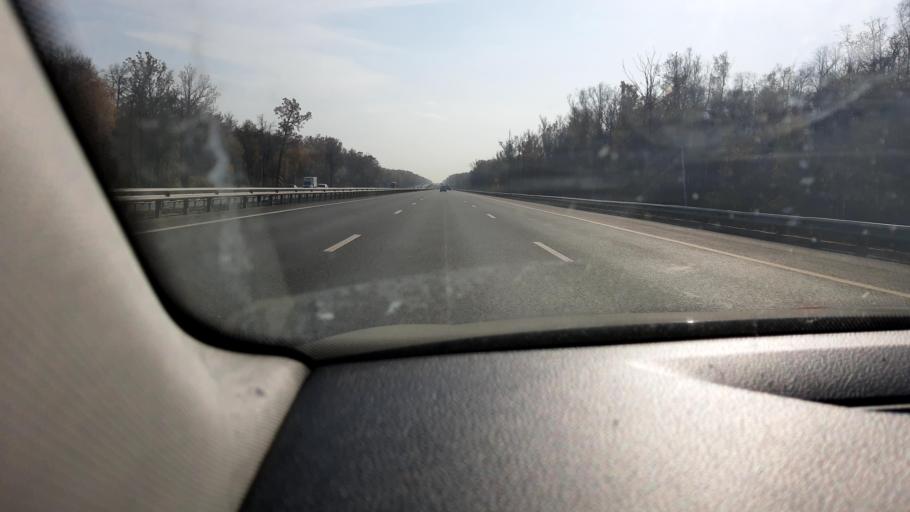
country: RU
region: Moskovskaya
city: Stupino
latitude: 54.9263
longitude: 37.9976
